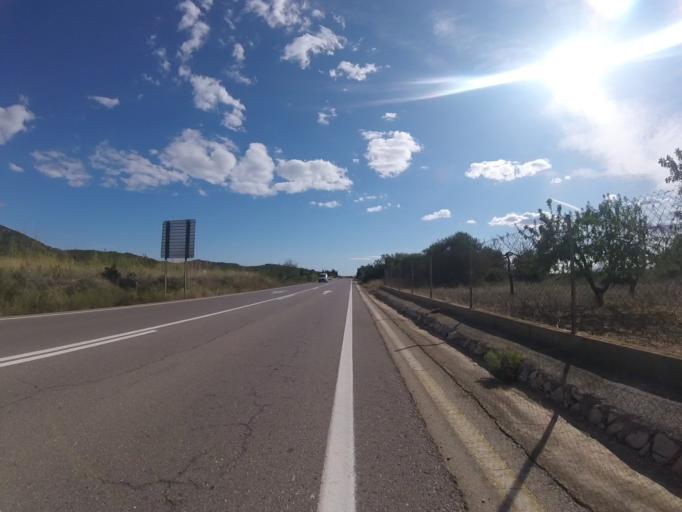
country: ES
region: Valencia
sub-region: Provincia de Castello
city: Alcala de Xivert
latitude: 40.2643
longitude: 0.2424
